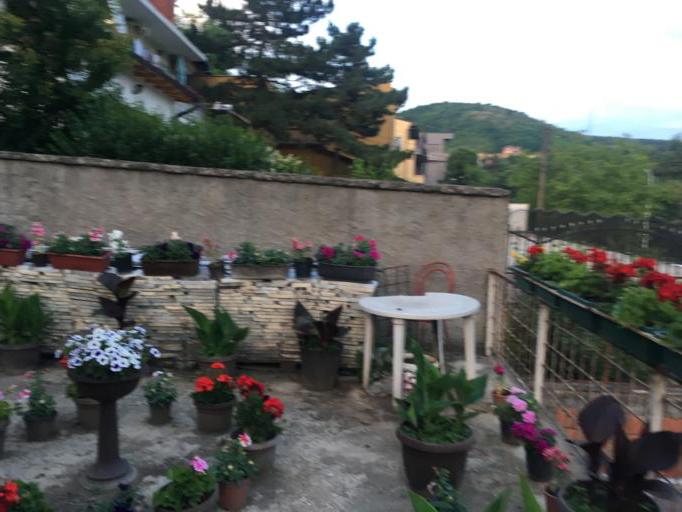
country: XK
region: Pristina
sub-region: Komuna e Prishtines
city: Pristina
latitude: 42.6662
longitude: 21.1820
